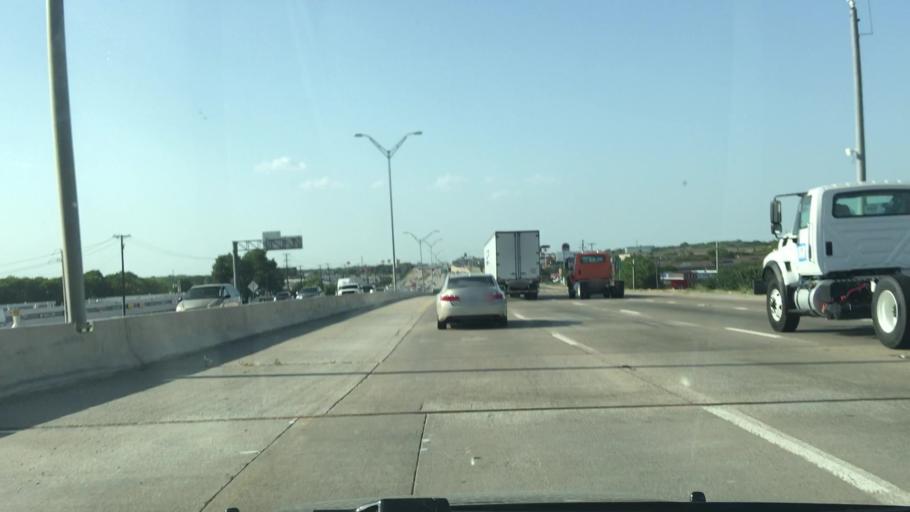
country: US
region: Texas
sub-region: Dallas County
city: DeSoto
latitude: 32.5909
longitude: -96.8224
